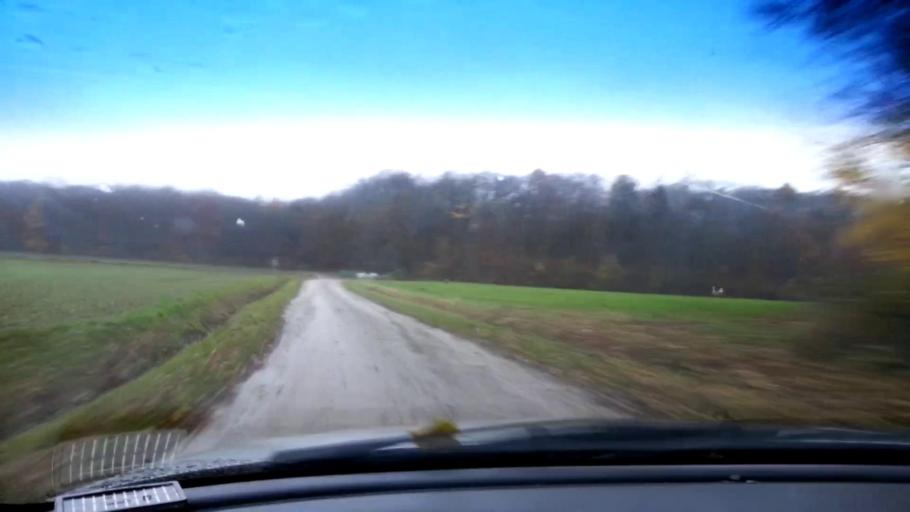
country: DE
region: Bavaria
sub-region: Upper Franconia
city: Schesslitz
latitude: 49.9462
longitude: 11.0287
